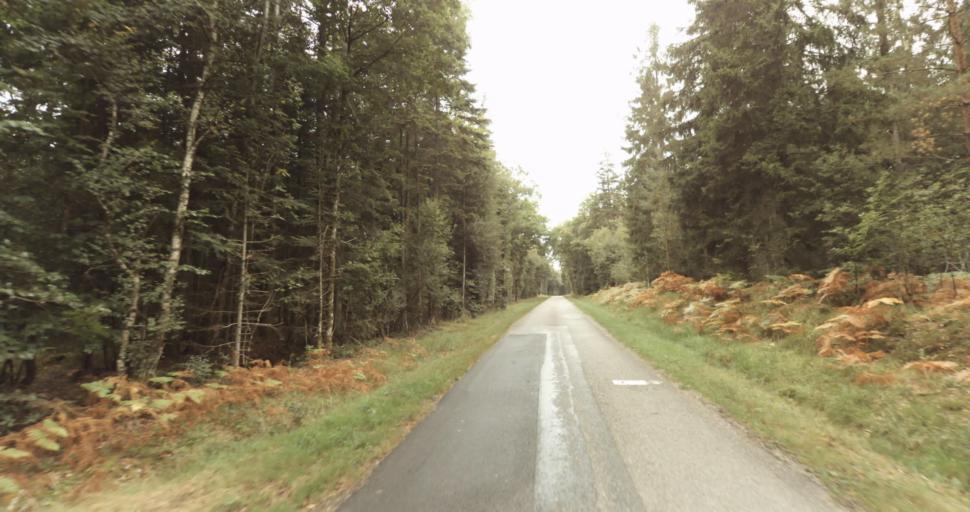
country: FR
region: Lower Normandy
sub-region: Departement de l'Orne
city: Gace
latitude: 48.8214
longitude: 0.3385
